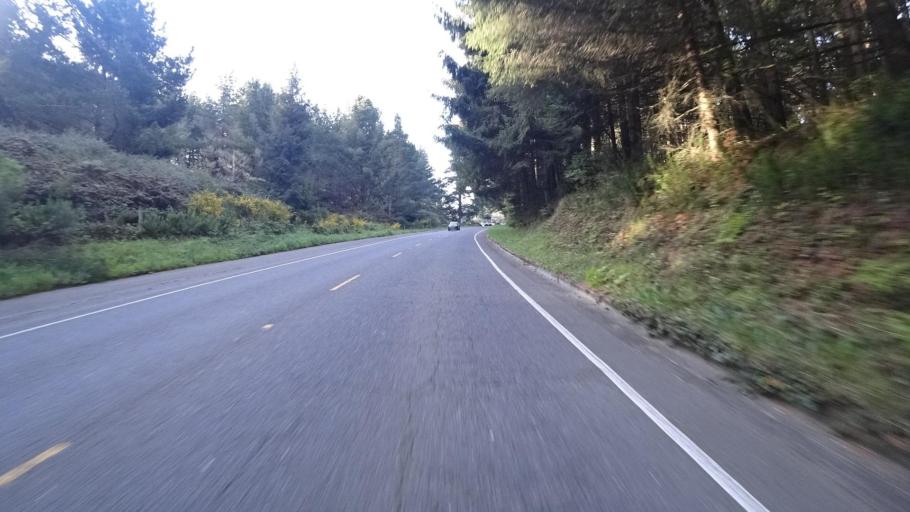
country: US
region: California
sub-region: Humboldt County
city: Humboldt Hill
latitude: 40.7245
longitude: -124.2014
